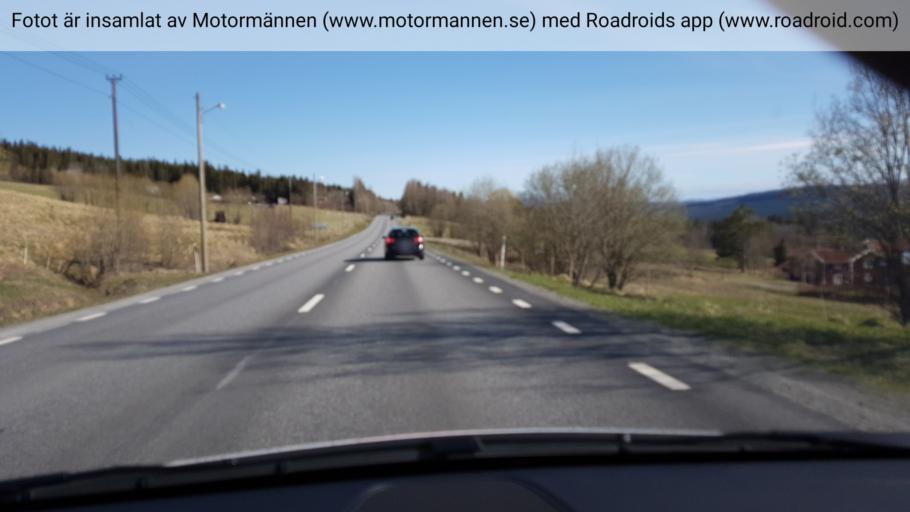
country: SE
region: Jaemtland
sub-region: Are Kommun
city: Are
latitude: 63.3636
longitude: 13.1732
